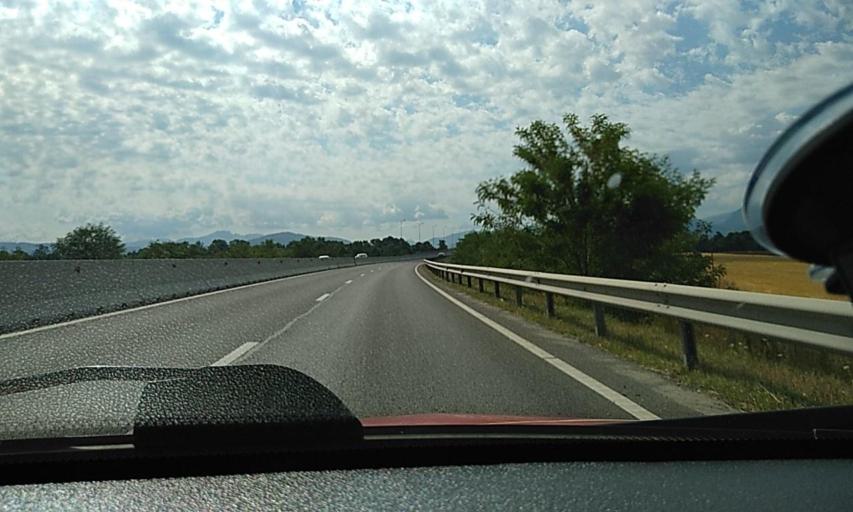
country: RO
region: Brasov
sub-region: Comuna Harman
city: Harman
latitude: 45.6792
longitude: 25.6675
